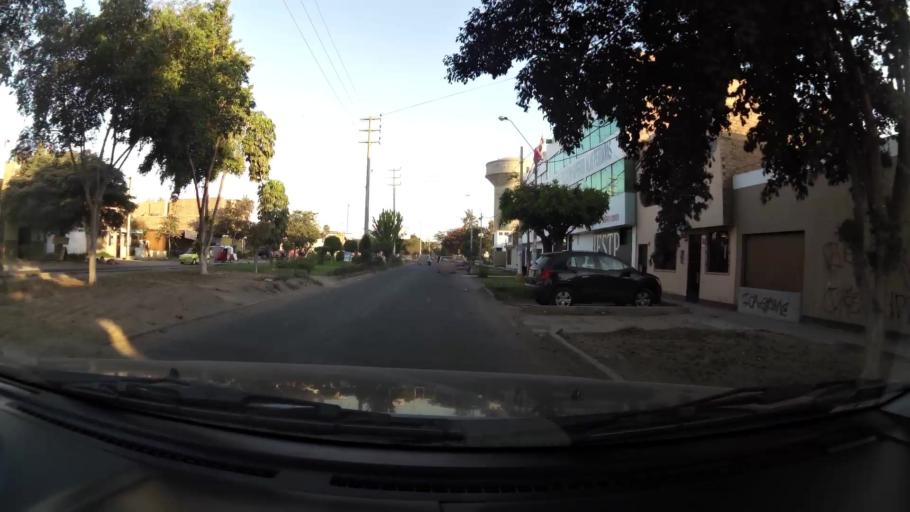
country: PE
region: Ica
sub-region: Provincia de Ica
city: Ica
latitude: -14.0754
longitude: -75.7234
